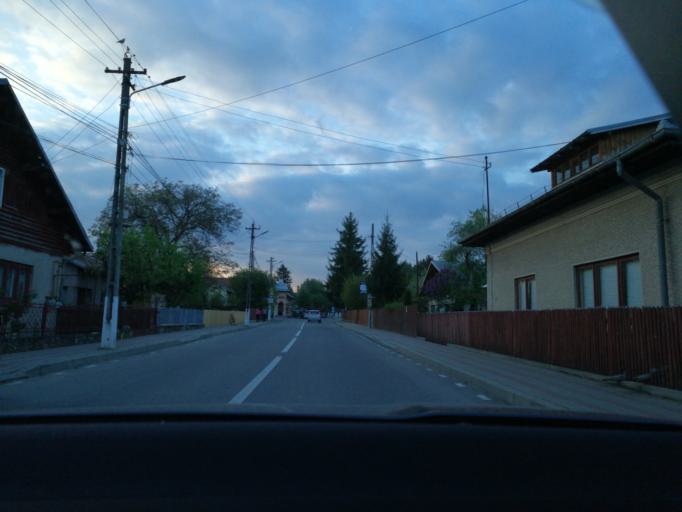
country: RO
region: Prahova
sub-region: Comuna Cornu
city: Cornu de Jos
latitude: 45.1539
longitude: 25.7040
